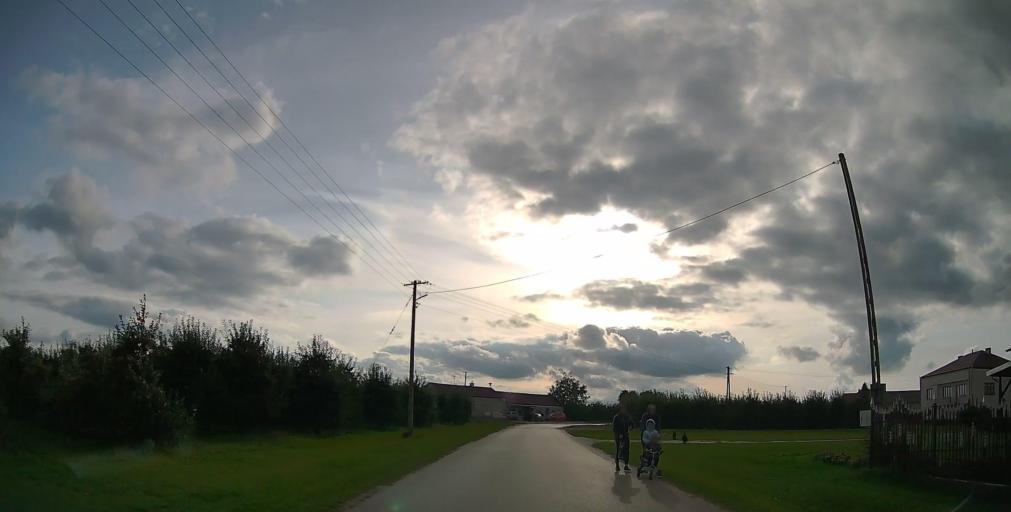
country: PL
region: Masovian Voivodeship
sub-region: Powiat grojecki
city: Jasieniec
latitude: 51.7546
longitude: 20.9199
